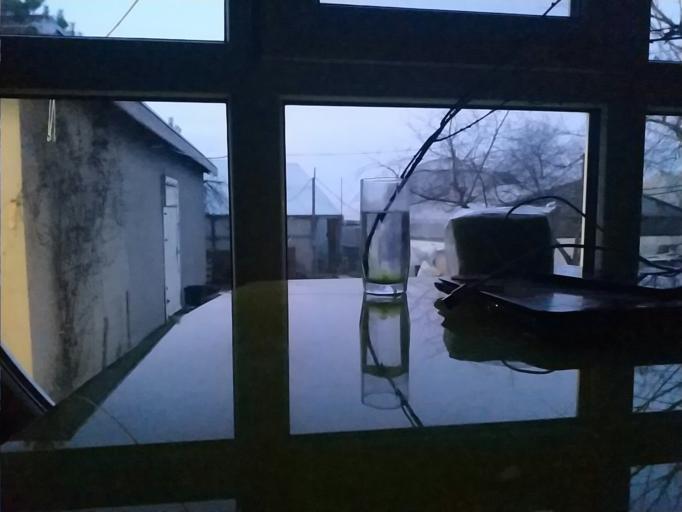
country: RU
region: Republic of Karelia
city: Sukkozero
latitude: 62.8367
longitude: 31.8273
